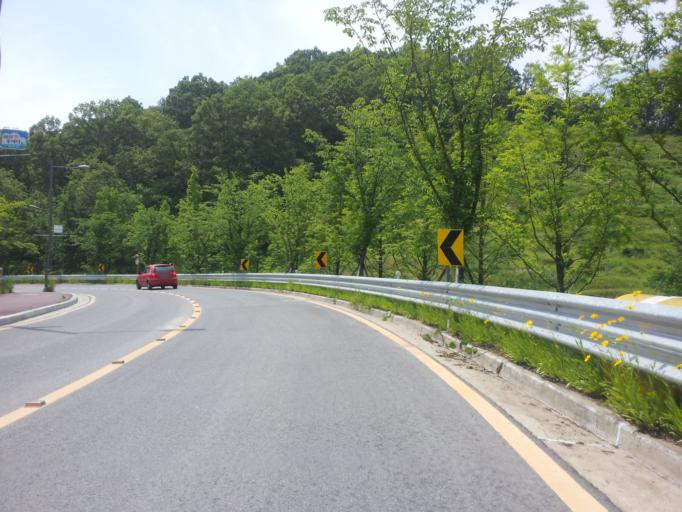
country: KR
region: Daejeon
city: Sintansin
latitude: 36.4576
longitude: 127.4748
